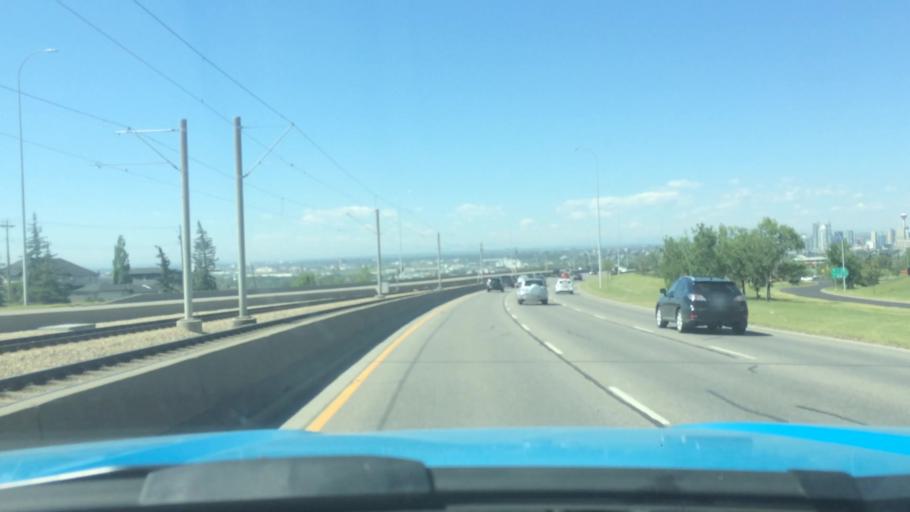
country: CA
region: Alberta
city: Calgary
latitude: 51.0469
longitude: -113.9969
